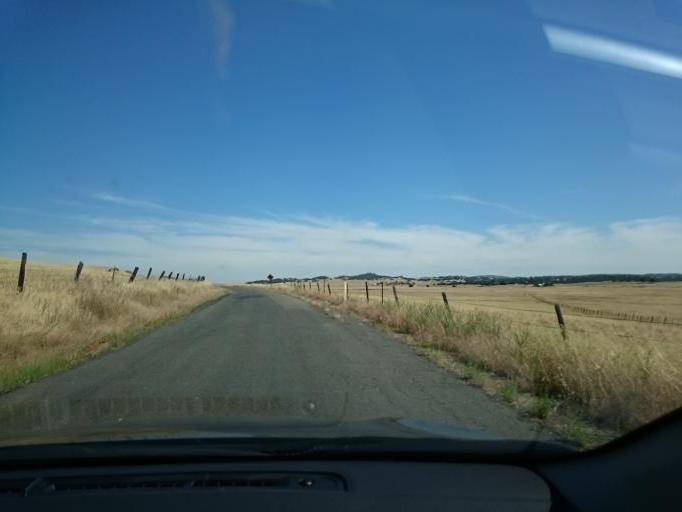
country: US
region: California
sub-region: Calaveras County
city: Copperopolis
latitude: 38.0513
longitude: -120.7229
